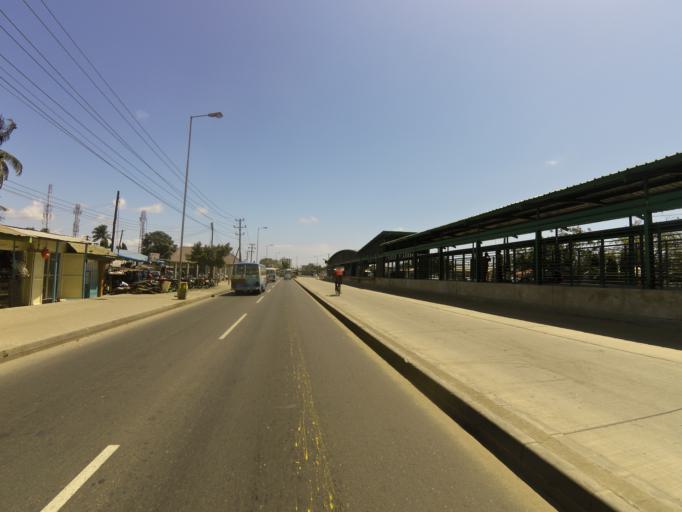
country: TZ
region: Dar es Salaam
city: Magomeni
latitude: -6.7956
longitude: 39.2641
